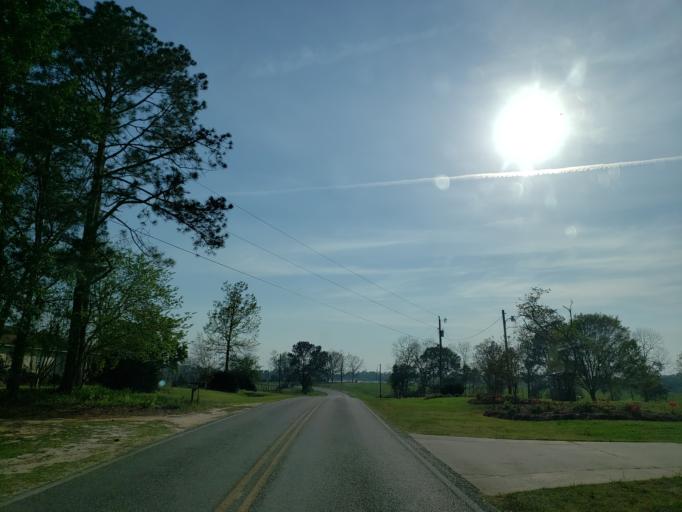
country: US
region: Georgia
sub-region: Tift County
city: Tifton
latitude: 31.5328
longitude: -83.5569
